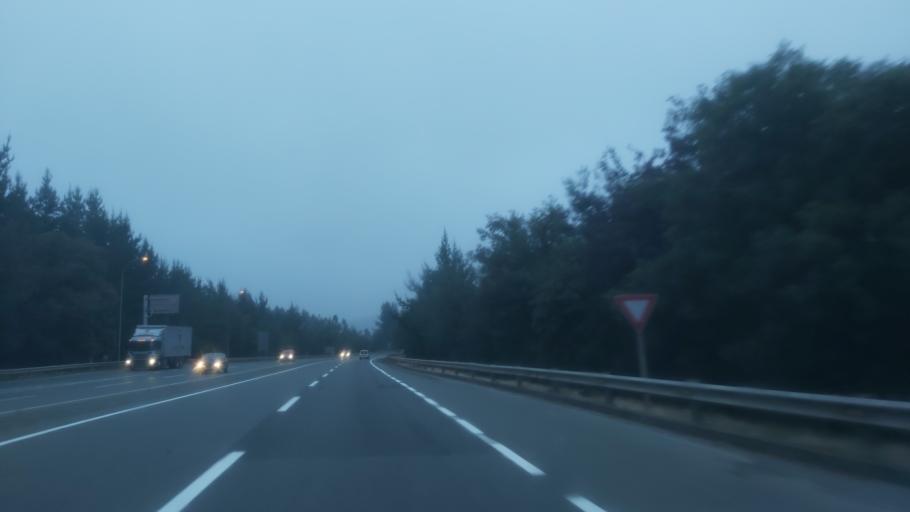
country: CL
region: Biobio
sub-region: Provincia de Concepcion
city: Penco
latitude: -36.7367
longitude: -72.8905
